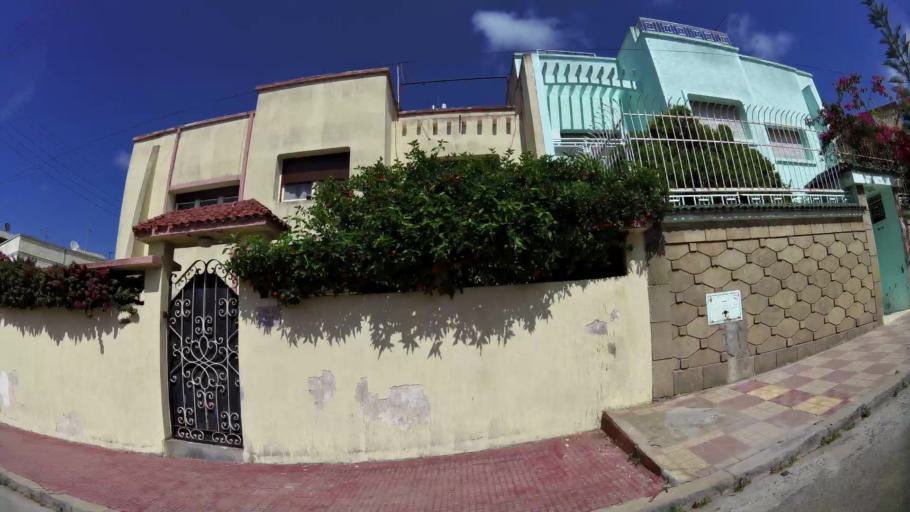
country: MA
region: Rabat-Sale-Zemmour-Zaer
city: Sale
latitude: 34.0365
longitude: -6.7950
